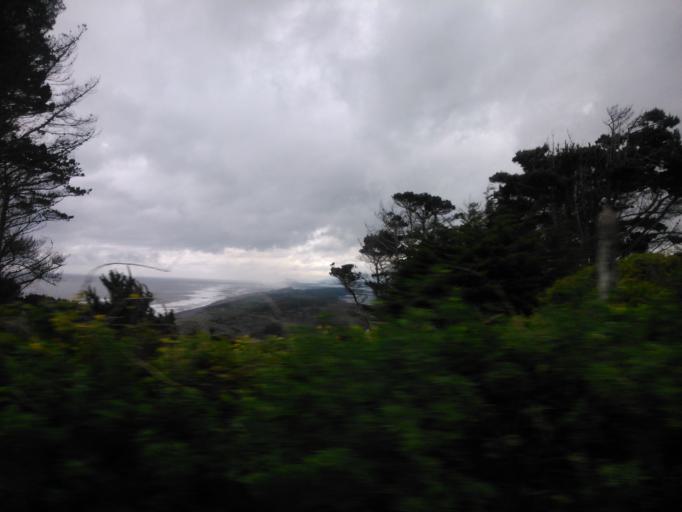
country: CL
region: Araucania
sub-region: Provincia de Cautin
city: Carahue
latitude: -38.8156
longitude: -73.3981
